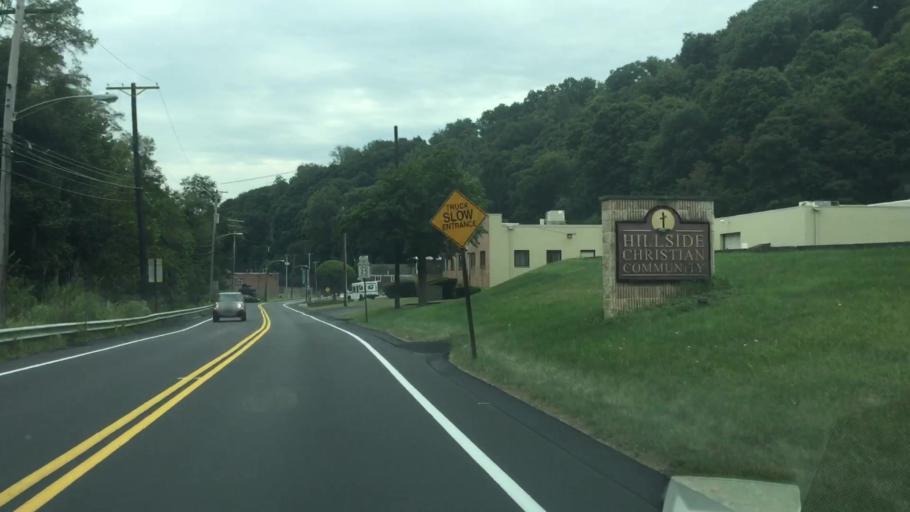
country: US
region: Pennsylvania
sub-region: Allegheny County
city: Carnegie
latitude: 40.4160
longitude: -80.0990
